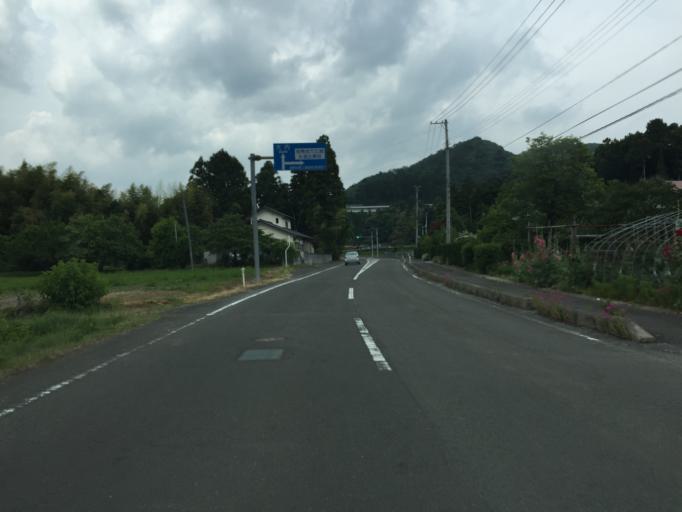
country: JP
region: Miyagi
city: Marumori
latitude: 37.8227
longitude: 140.8791
